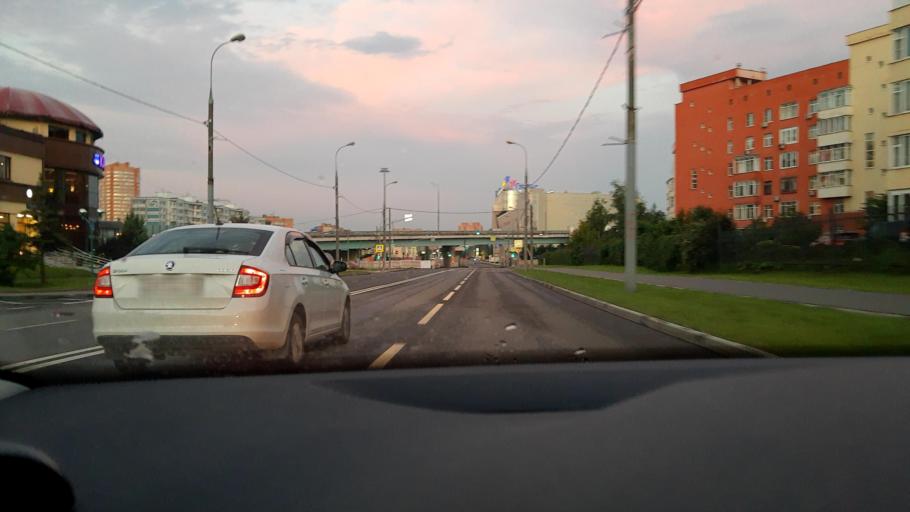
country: RU
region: Moscow
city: Khimki
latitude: 55.8873
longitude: 37.4016
